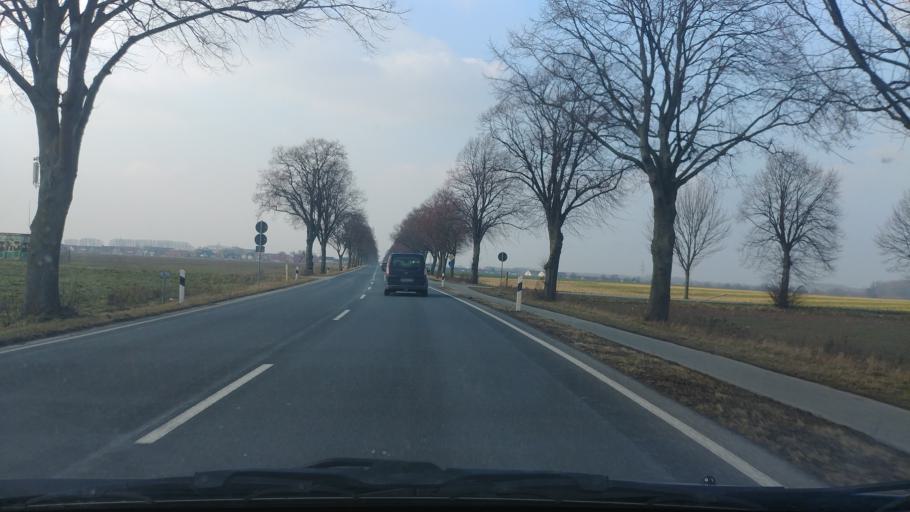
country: DE
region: Lower Saxony
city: Pattensen
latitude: 52.2885
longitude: 9.7538
